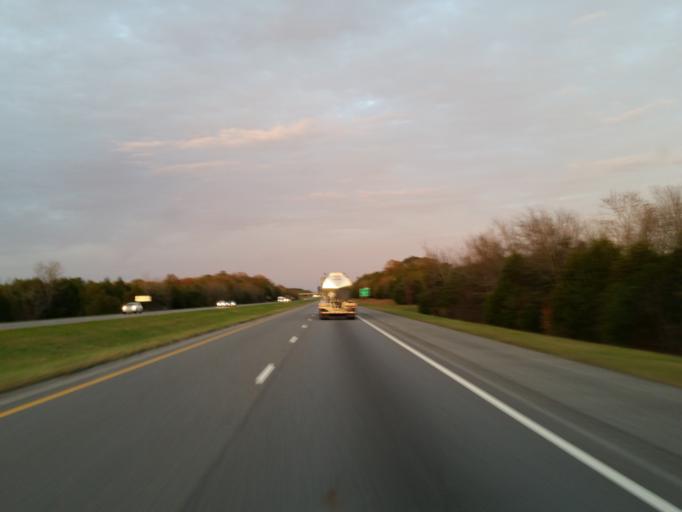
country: US
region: Alabama
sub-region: Sumter County
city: Livingston
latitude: 32.6898
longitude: -88.1543
